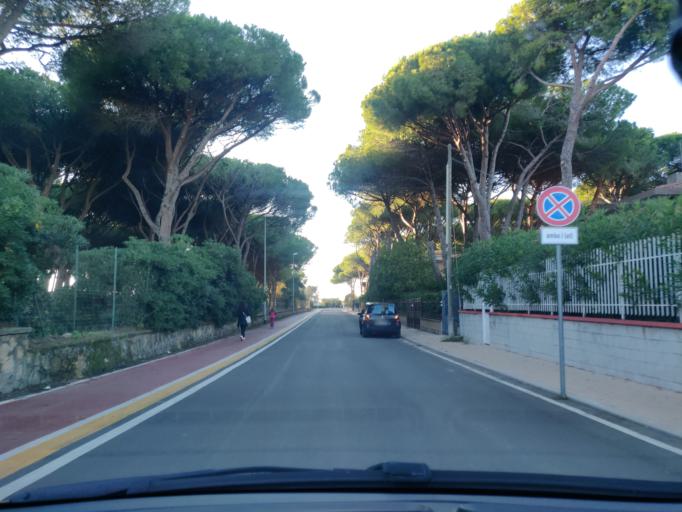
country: IT
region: Latium
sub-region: Provincia di Viterbo
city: Tarquinia
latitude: 42.2163
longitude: 11.7111
